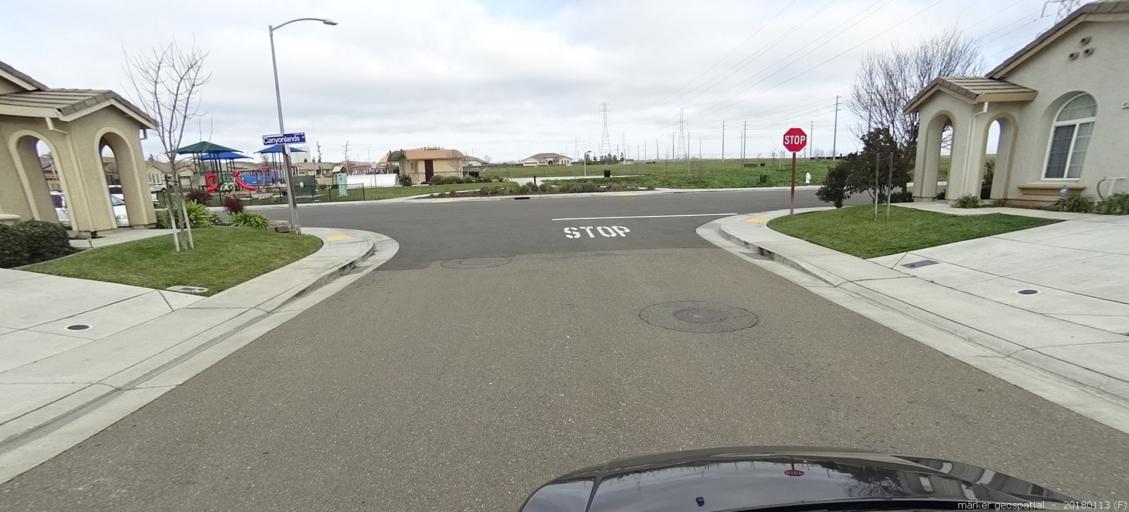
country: US
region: California
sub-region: Sacramento County
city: Gold River
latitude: 38.5555
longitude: -121.2081
